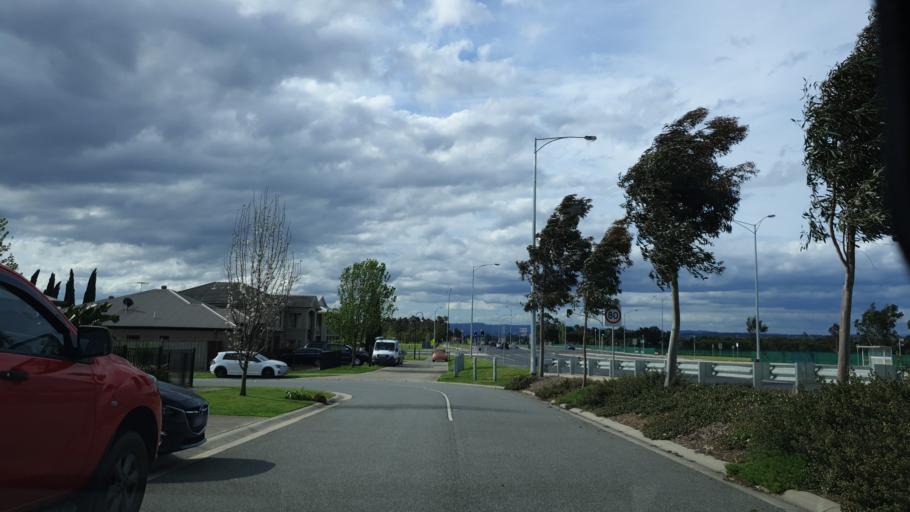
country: AU
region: Victoria
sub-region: Casey
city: Cranbourne North
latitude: -38.0731
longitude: 145.2974
